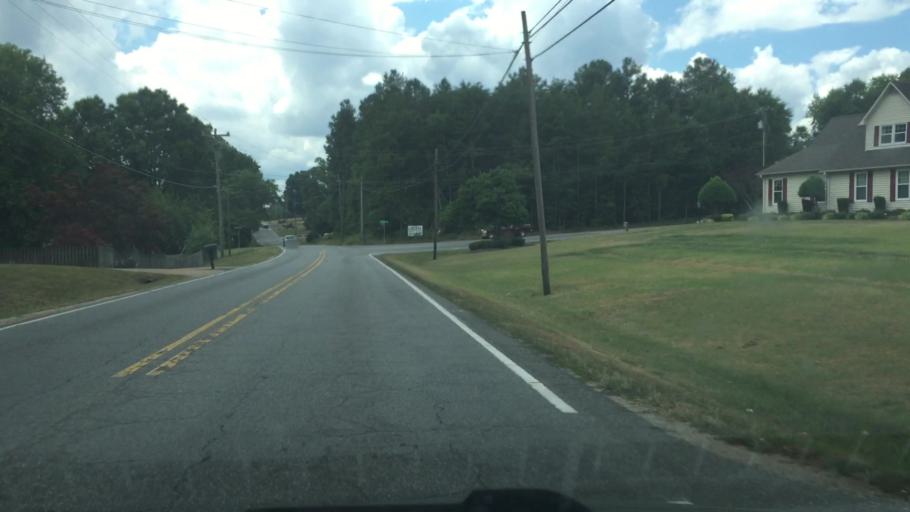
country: US
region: North Carolina
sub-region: Rowan County
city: Enochville
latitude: 35.5142
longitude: -80.6713
